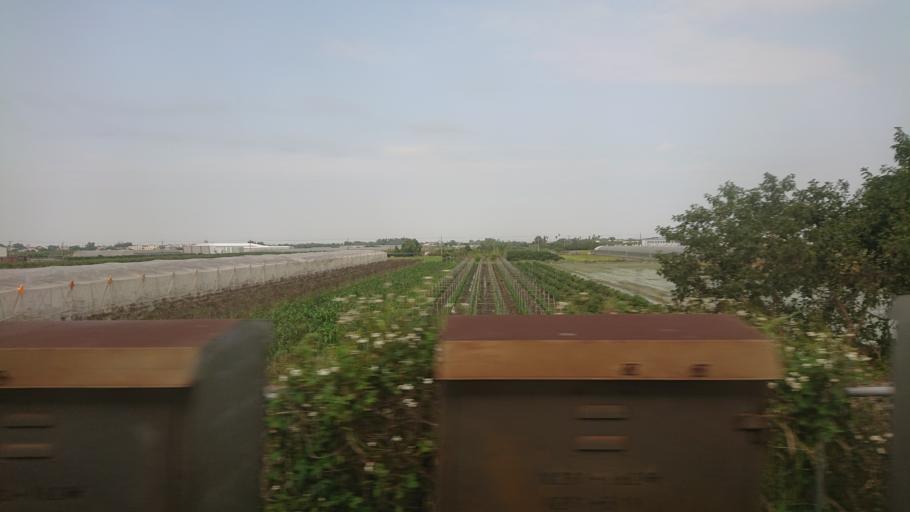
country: TW
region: Taiwan
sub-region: Yunlin
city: Douliu
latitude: 23.7340
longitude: 120.5821
